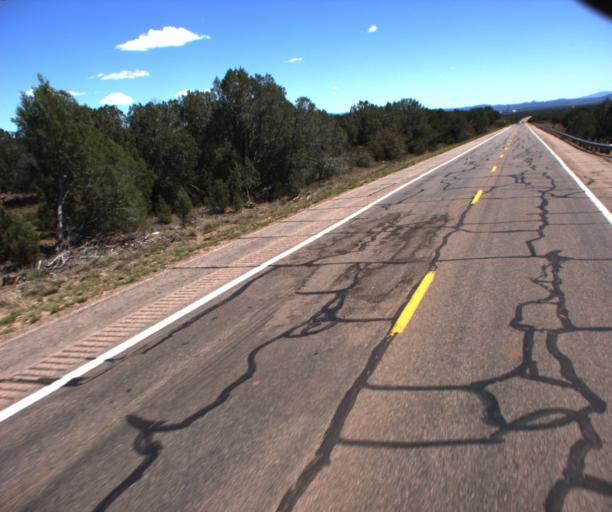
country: US
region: Arizona
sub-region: Yavapai County
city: Paulden
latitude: 35.0635
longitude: -112.3996
